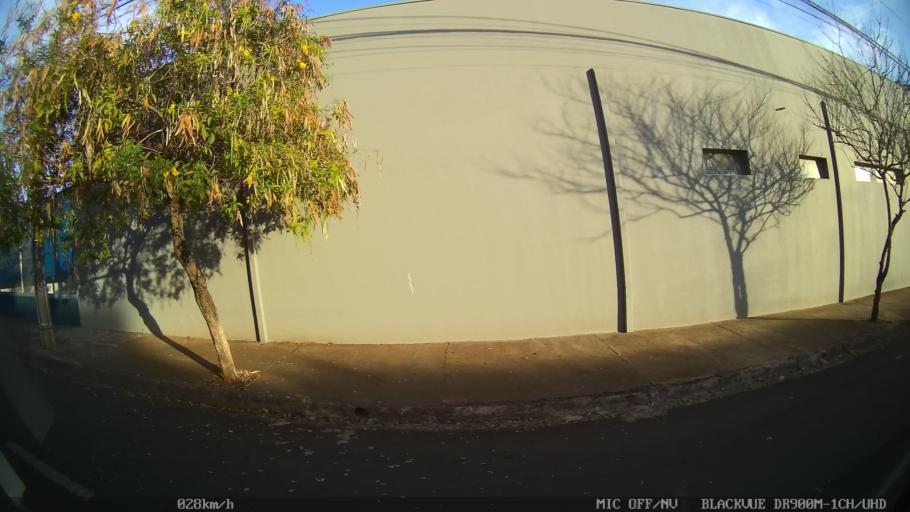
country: BR
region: Sao Paulo
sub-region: Franca
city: Franca
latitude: -20.5367
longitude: -47.3873
